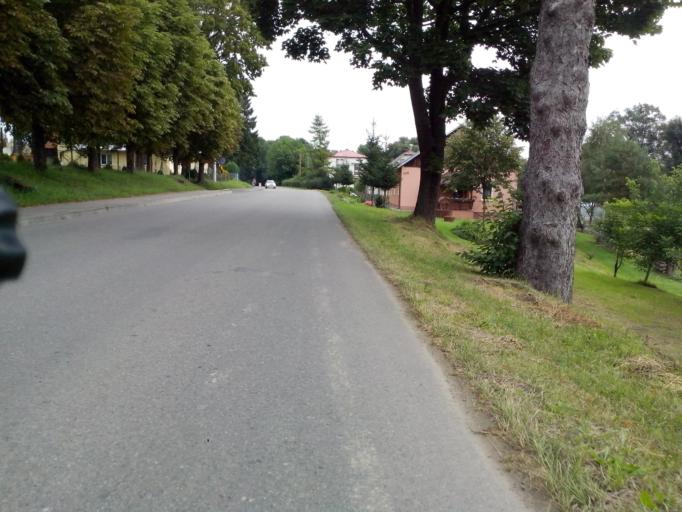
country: PL
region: Subcarpathian Voivodeship
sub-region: Powiat brzozowski
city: Jasienica Rosielna
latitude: 49.7540
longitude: 21.9471
